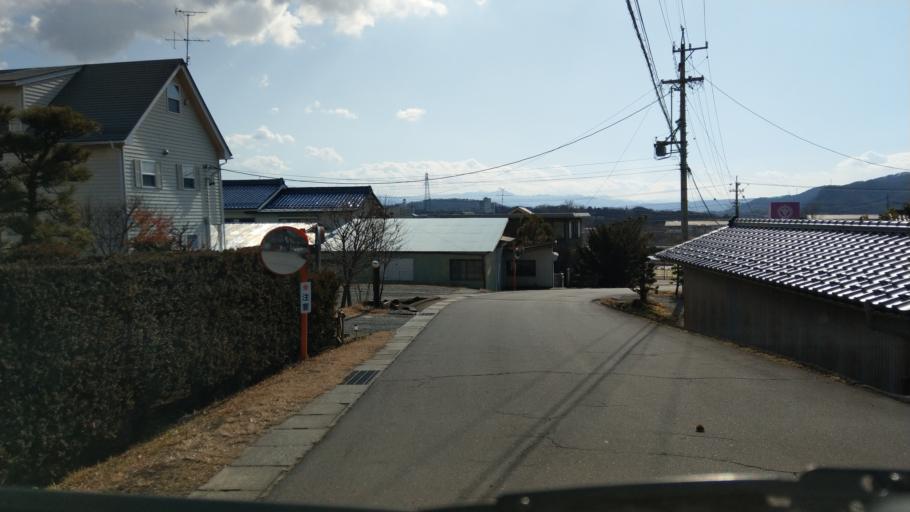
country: JP
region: Nagano
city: Komoro
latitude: 36.3388
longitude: 138.4128
